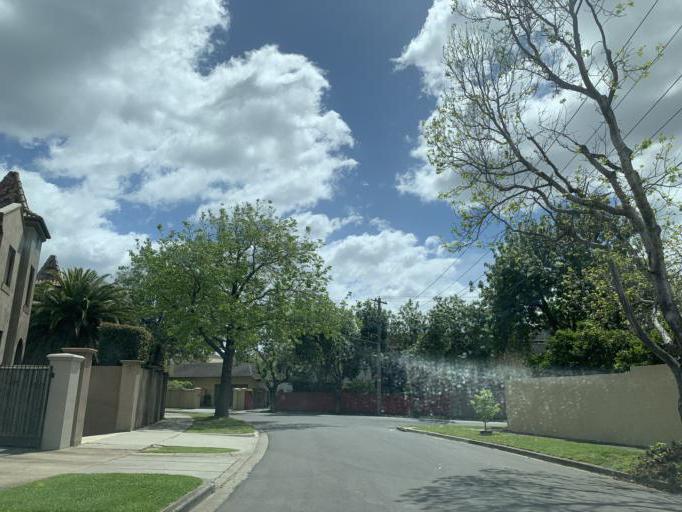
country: AU
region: Victoria
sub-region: Bayside
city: North Brighton
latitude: -37.9020
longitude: 144.9899
